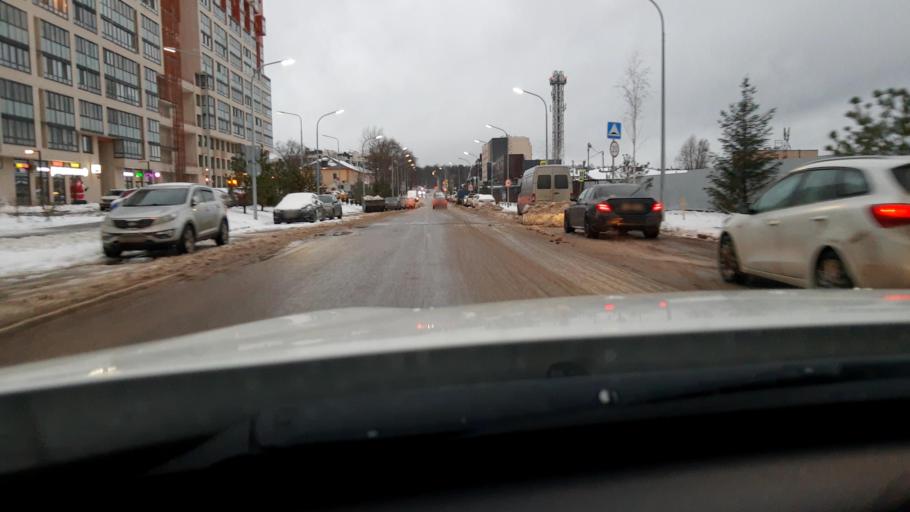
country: RU
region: Moskovskaya
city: Krasnogorsk
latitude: 55.8731
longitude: 37.3169
